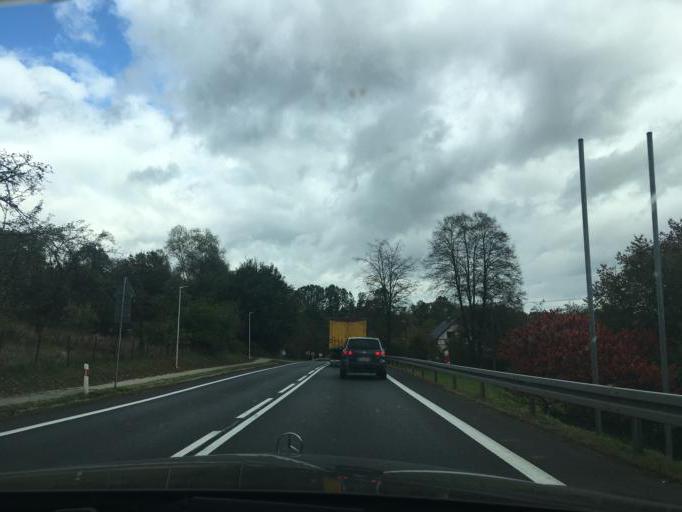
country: PL
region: Subcarpathian Voivodeship
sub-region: Powiat strzyzowski
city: Babica
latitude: 49.9149
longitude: 21.8689
